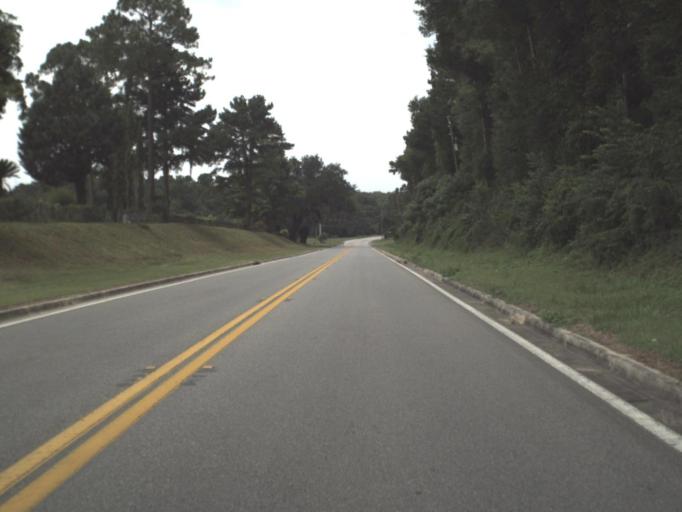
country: US
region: Florida
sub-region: Madison County
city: Madison
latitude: 30.4751
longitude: -83.4155
